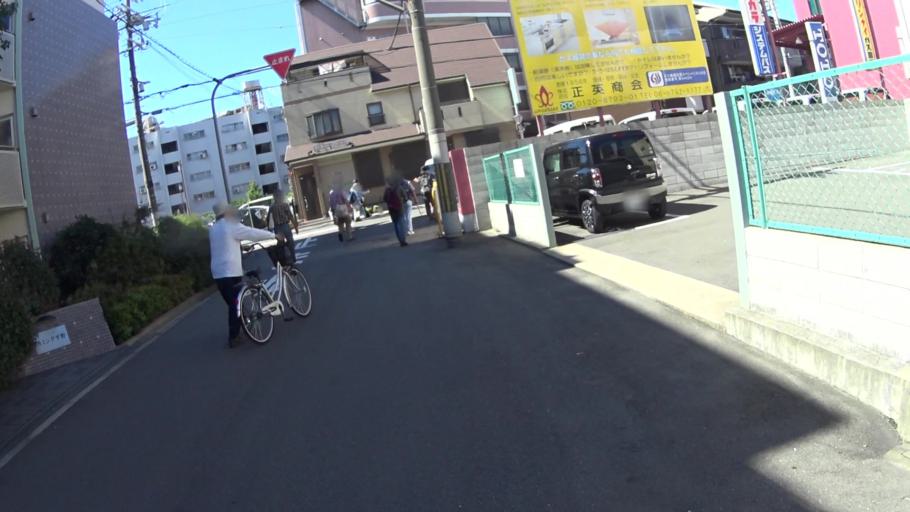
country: JP
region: Osaka
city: Yao
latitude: 34.6319
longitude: 135.5557
